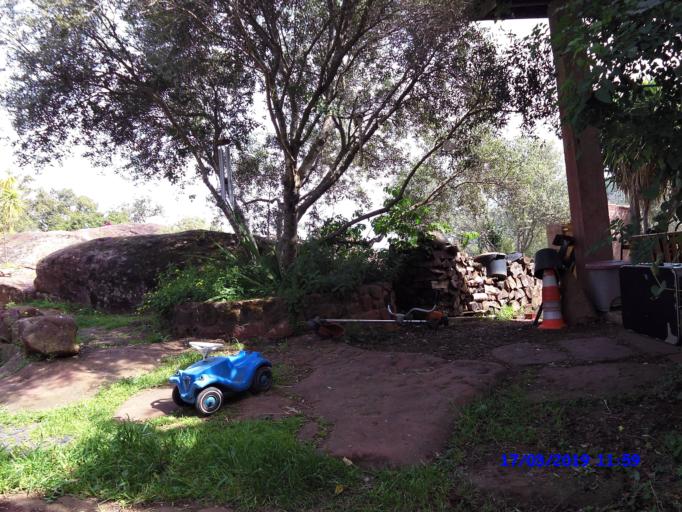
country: PT
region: Faro
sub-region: Silves
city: Sao Bartolomeu de Messines
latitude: 37.2540
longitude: -8.3481
